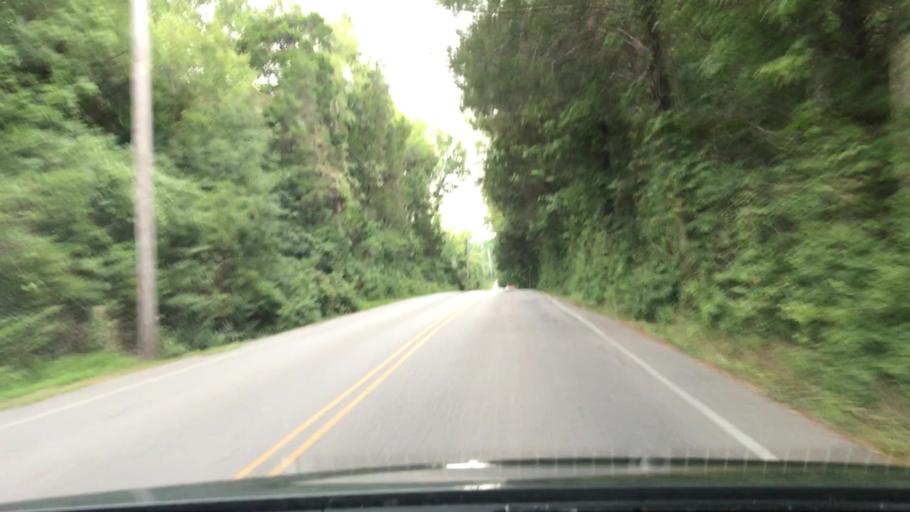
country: US
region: Tennessee
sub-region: Williamson County
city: Nolensville
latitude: 35.9687
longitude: -86.6233
